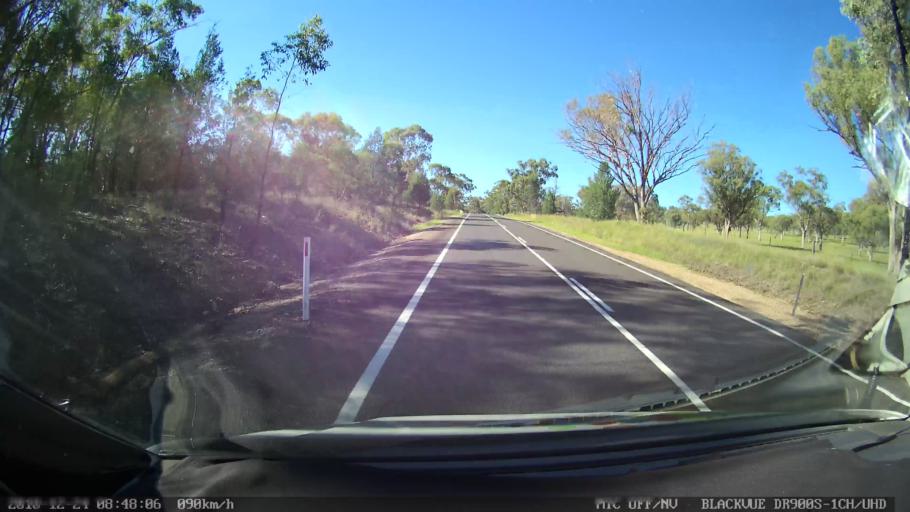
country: AU
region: New South Wales
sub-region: Liverpool Plains
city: Quirindi
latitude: -31.4510
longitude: 150.6460
